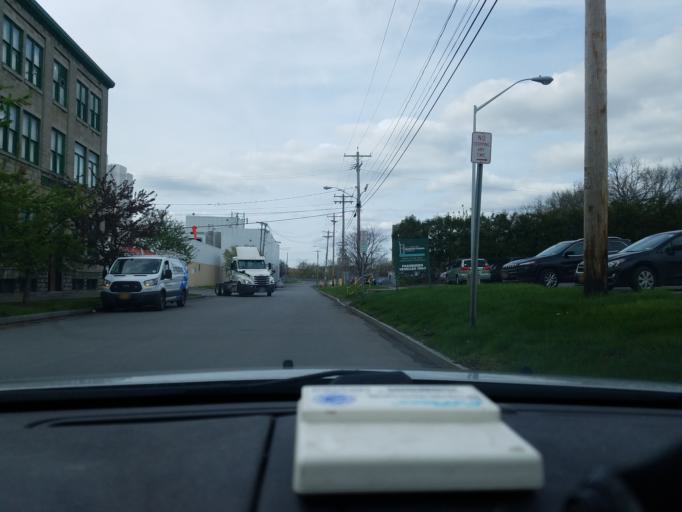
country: US
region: New York
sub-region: Onondaga County
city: Syracuse
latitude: 43.0409
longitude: -76.1531
